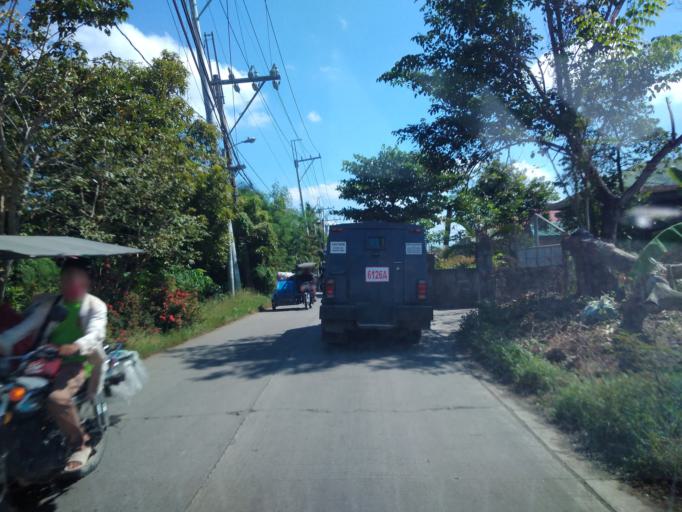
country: PH
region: Central Luzon
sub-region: Province of Bulacan
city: Balasing
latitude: 14.8579
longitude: 121.0186
